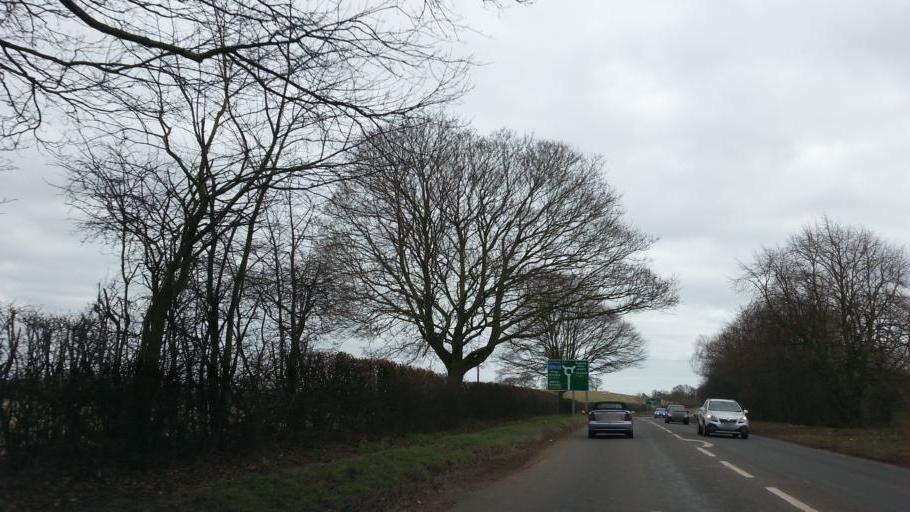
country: GB
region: England
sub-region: Staffordshire
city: Rugeley
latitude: 52.7769
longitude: -1.9557
